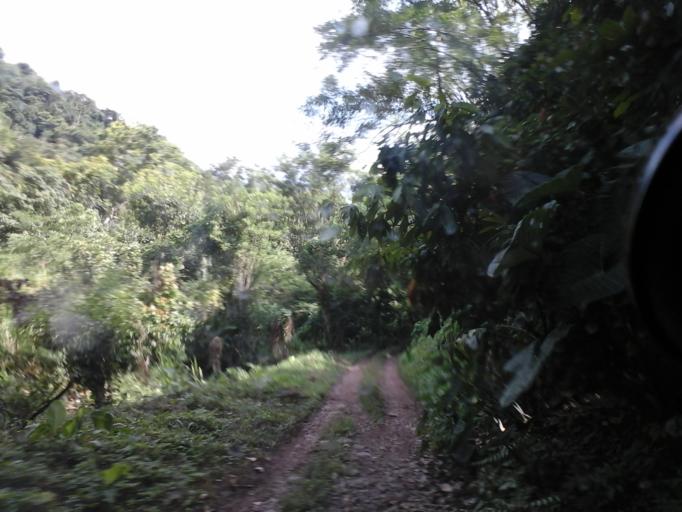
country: CO
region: Cesar
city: San Diego
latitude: 10.2836
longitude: -73.0883
